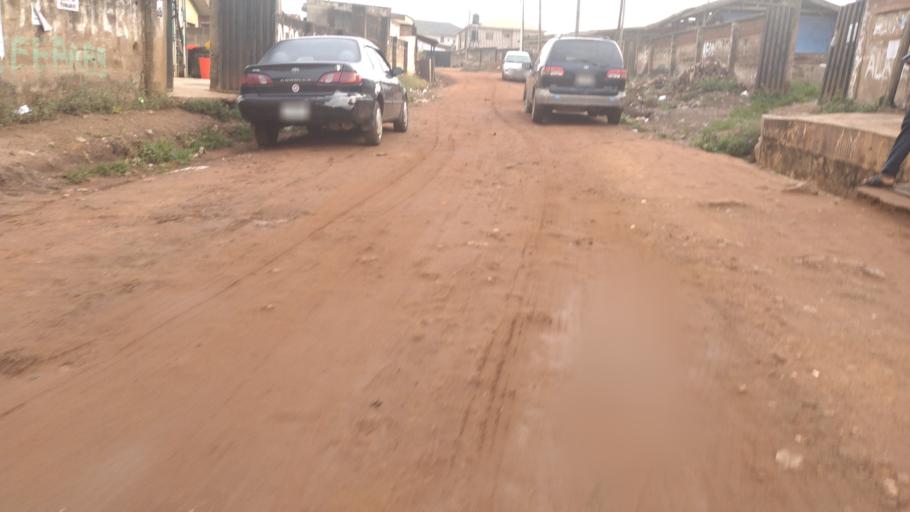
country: NG
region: Ondo
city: Akure
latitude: 7.2935
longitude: 5.1537
